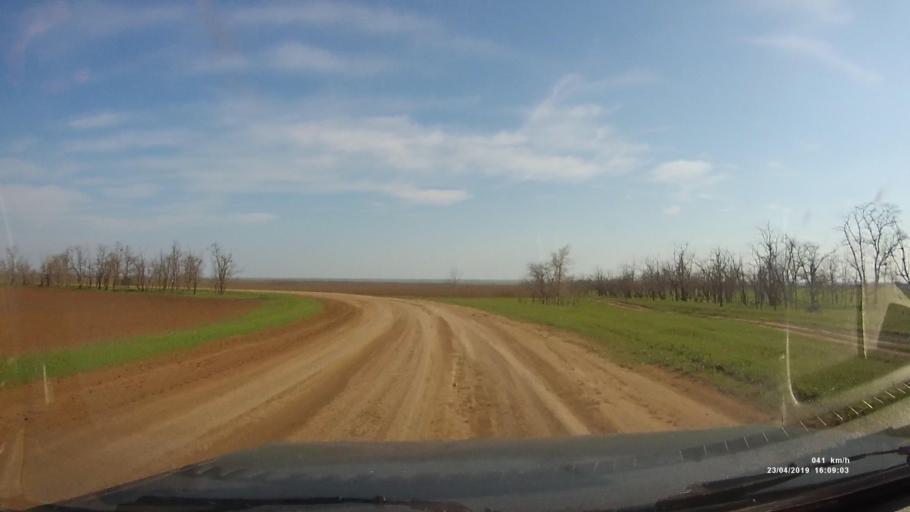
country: RU
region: Rostov
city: Remontnoye
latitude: 46.4823
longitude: 43.1076
